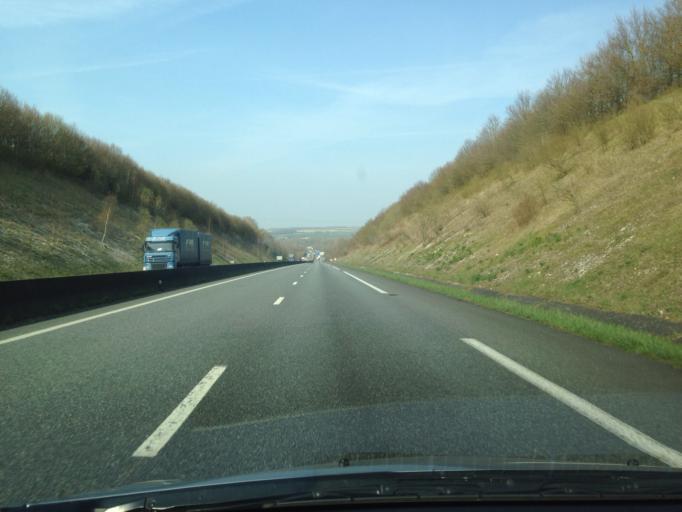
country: FR
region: Picardie
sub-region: Departement de la Somme
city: Abbeville
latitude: 50.0990
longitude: 1.7804
